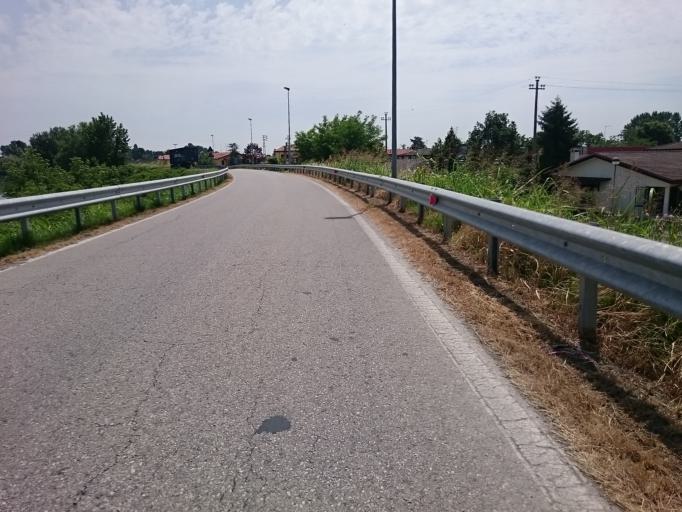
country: IT
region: Veneto
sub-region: Provincia di Padova
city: Codevigo
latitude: 45.2327
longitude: 12.1110
